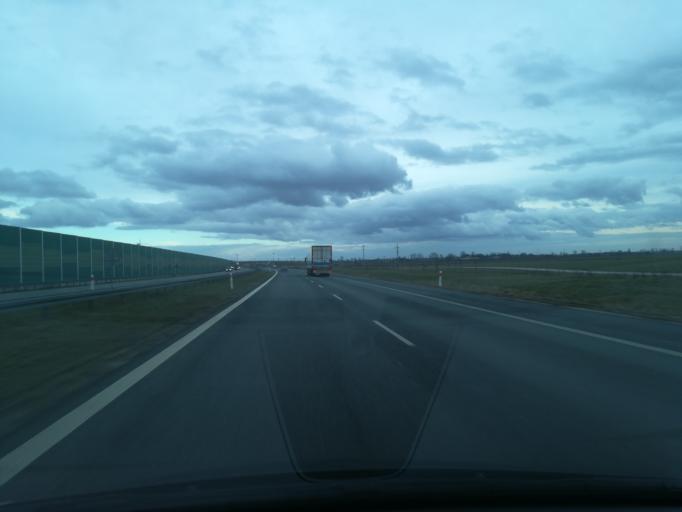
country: PL
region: Lodz Voivodeship
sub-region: Powiat kutnowski
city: Strzelce
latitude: 52.2733
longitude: 19.4175
